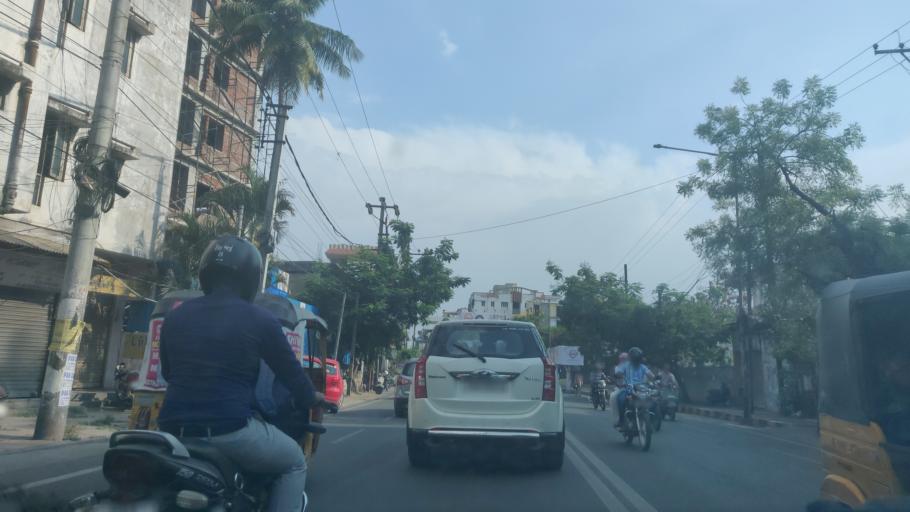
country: IN
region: Telangana
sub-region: Rangareddi
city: Gaddi Annaram
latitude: 17.3925
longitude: 78.5109
